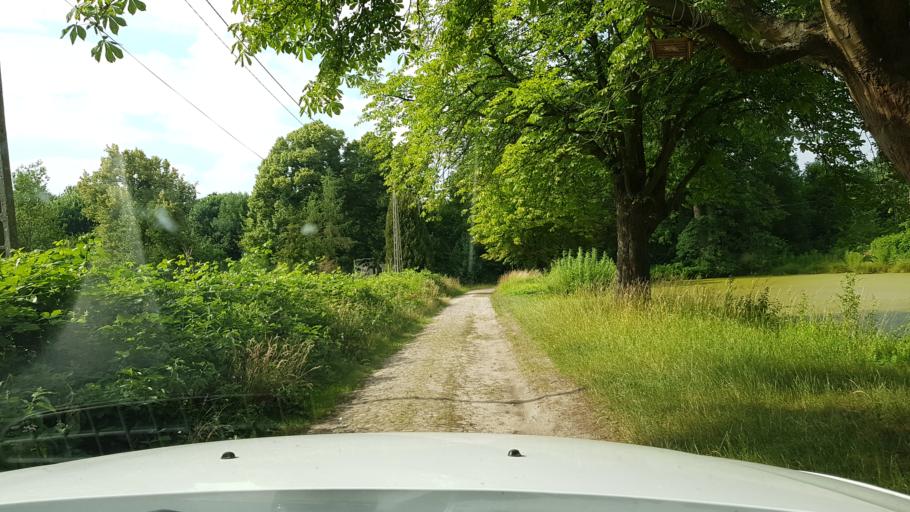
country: PL
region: West Pomeranian Voivodeship
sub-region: Powiat gryfinski
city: Moryn
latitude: 52.9196
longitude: 14.3617
